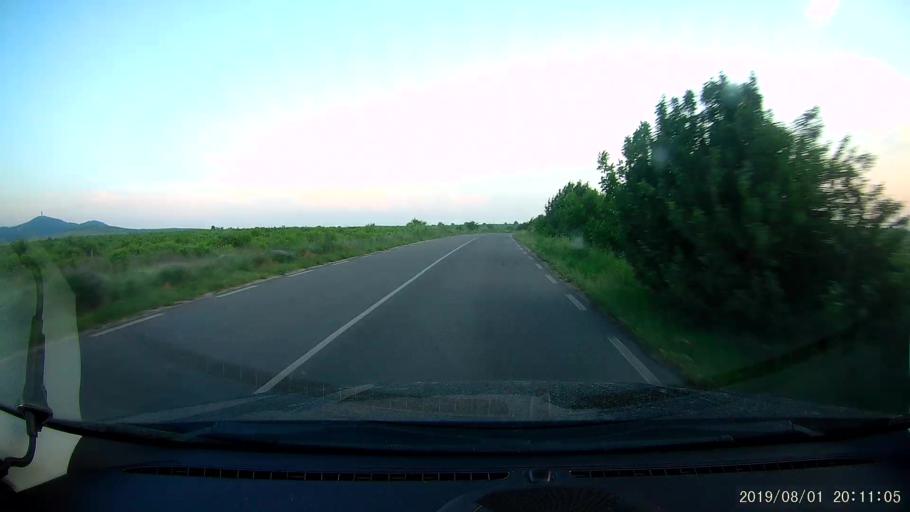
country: BG
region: Yambol
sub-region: Obshtina Yambol
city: Yambol
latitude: 42.4683
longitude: 26.6051
